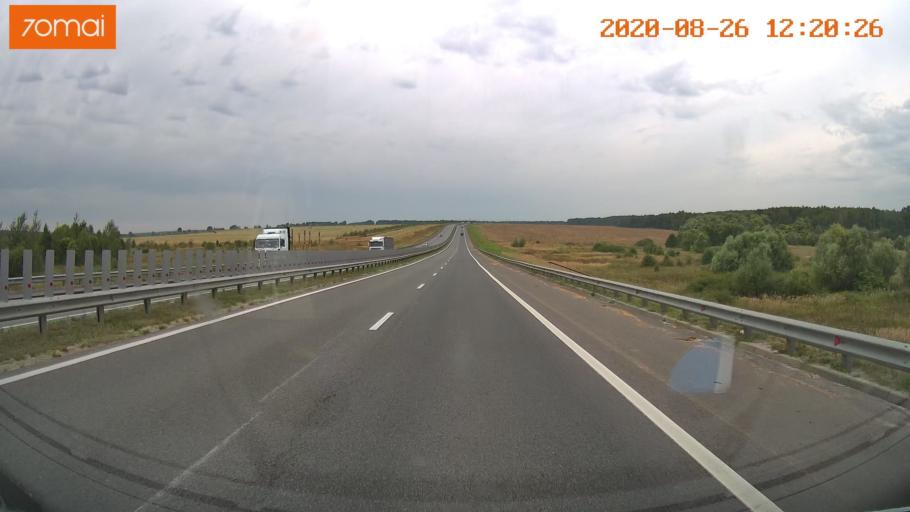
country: RU
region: Rjazan
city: Murmino
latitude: 54.4864
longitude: 39.9687
